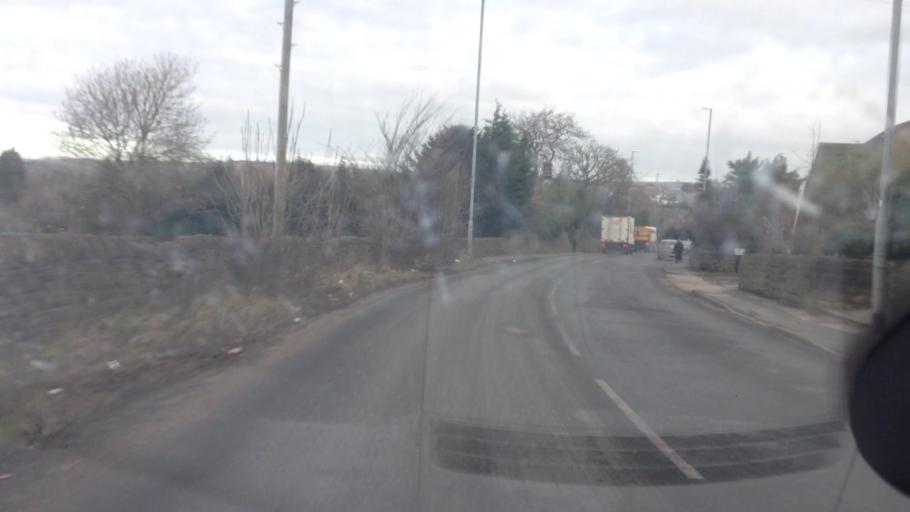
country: GB
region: England
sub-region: City and Borough of Leeds
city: Yeadon
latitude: 53.8556
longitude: -1.6919
